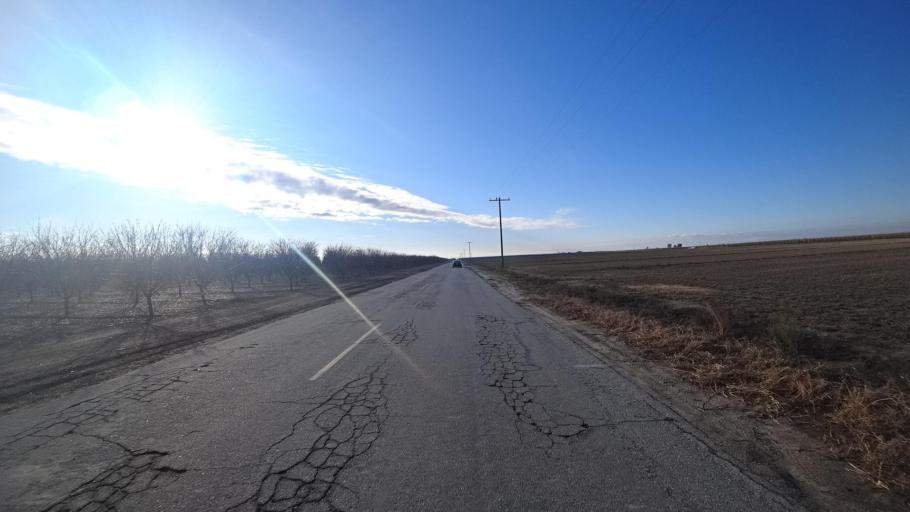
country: US
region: California
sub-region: Kern County
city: Delano
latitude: 35.7593
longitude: -119.3298
